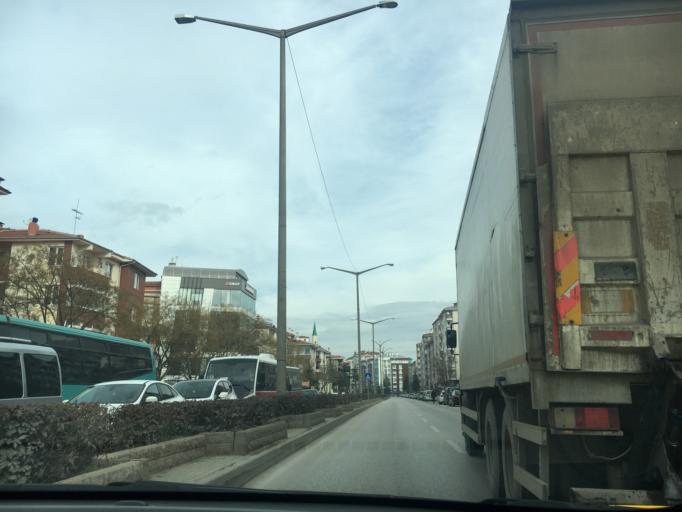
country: TR
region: Eskisehir
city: Eskisehir
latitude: 39.7677
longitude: 30.5010
